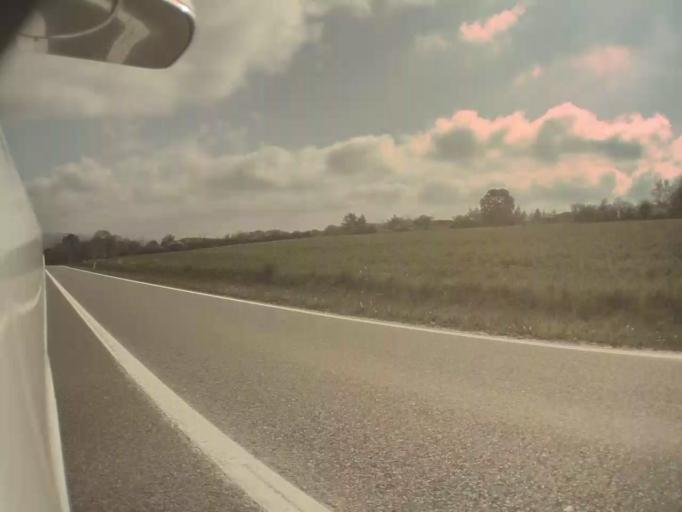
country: BE
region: Wallonia
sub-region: Province de Namur
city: Somme-Leuze
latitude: 50.3193
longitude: 5.3445
